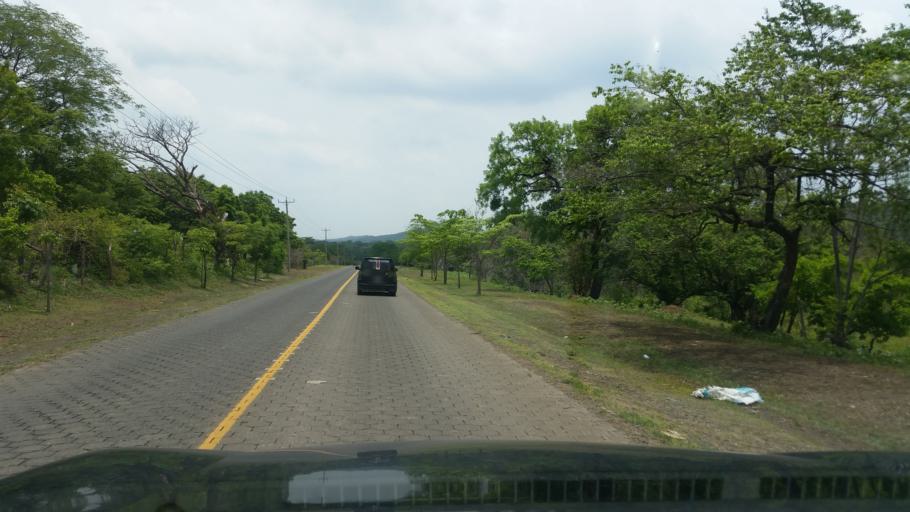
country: NI
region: Managua
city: Masachapa
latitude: 11.8375
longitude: -86.5120
